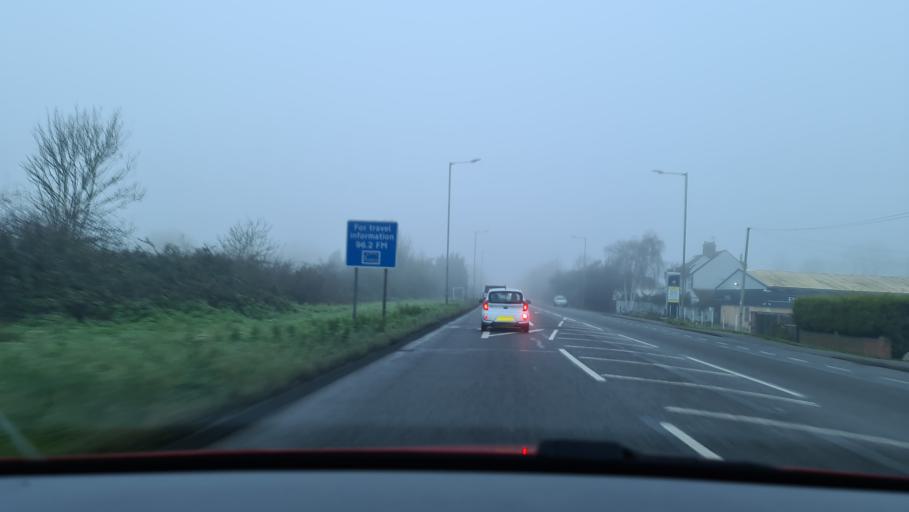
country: GB
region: England
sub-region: Buckinghamshire
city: Weston Turville
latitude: 51.8082
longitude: -0.7607
